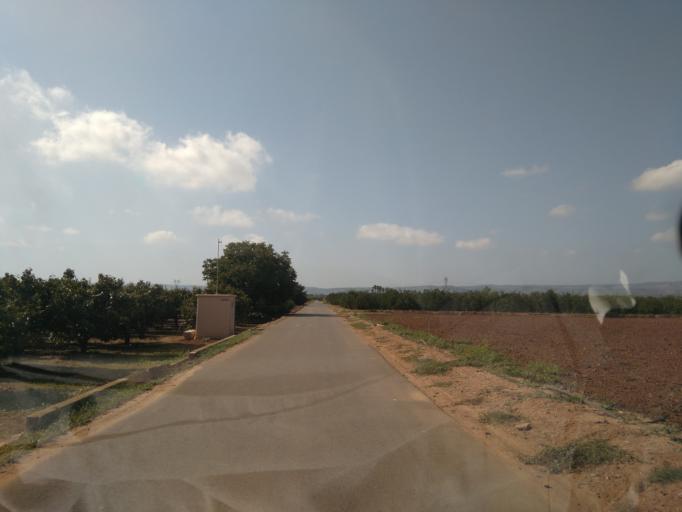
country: ES
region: Valencia
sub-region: Provincia de Valencia
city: Benimodo
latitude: 39.1858
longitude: -0.5355
